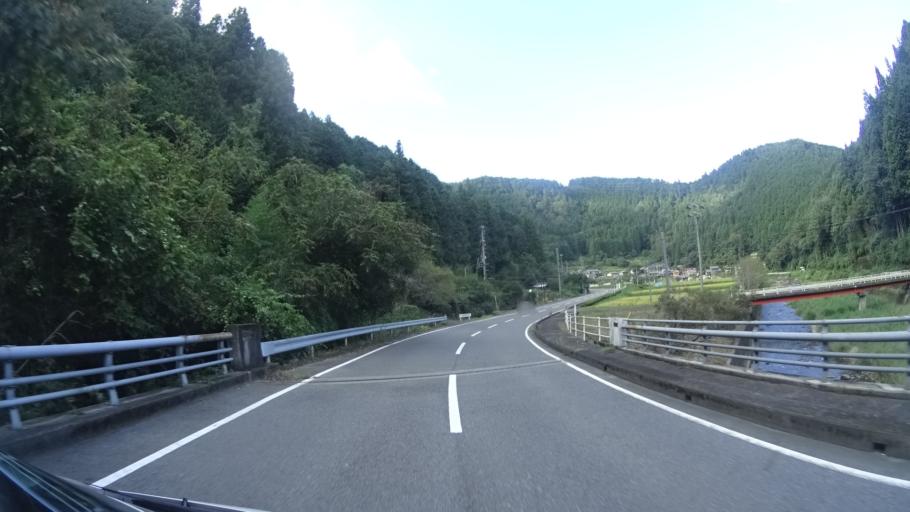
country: JP
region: Gifu
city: Minokamo
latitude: 35.5650
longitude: 137.1053
